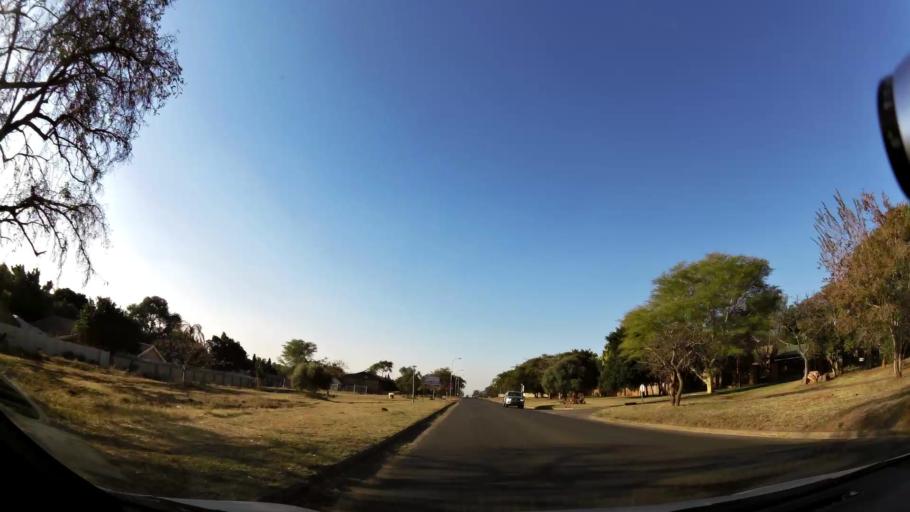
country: ZA
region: North-West
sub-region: Bojanala Platinum District Municipality
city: Rustenburg
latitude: -25.6859
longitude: 27.2395
